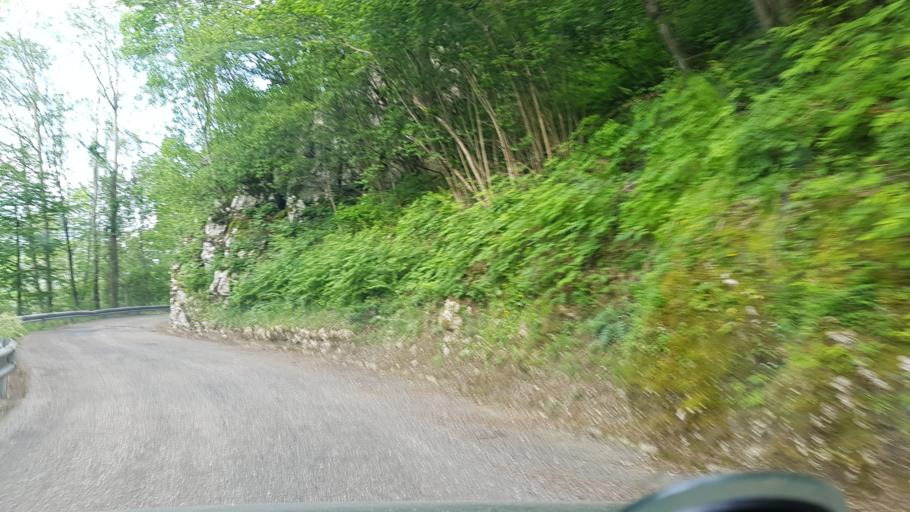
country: IT
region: Friuli Venezia Giulia
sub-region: Provincia di Udine
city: Pulfero
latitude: 46.1894
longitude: 13.4405
